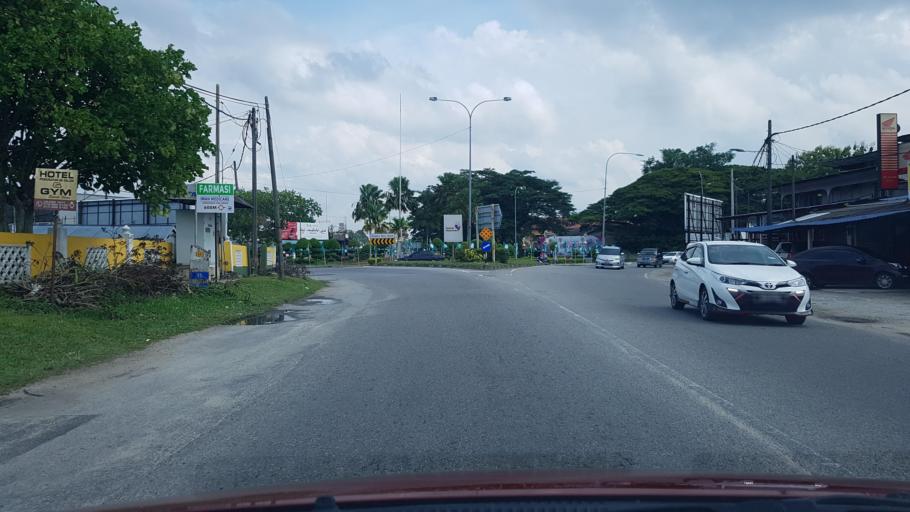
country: MY
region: Terengganu
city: Kuala Terengganu
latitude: 5.3483
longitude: 103.0926
